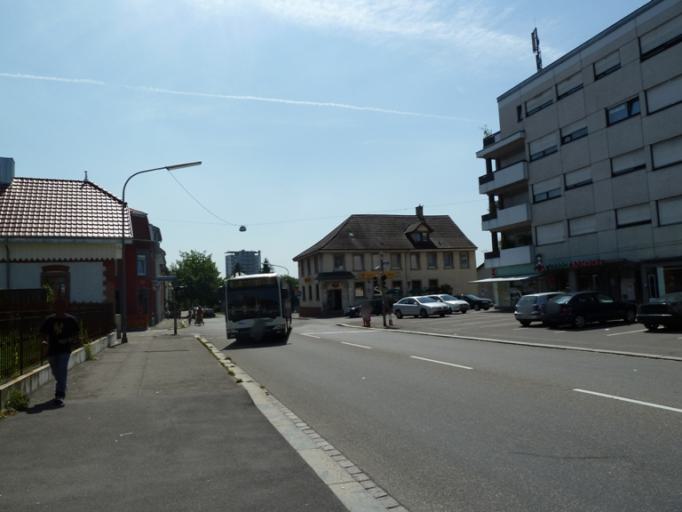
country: DE
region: Baden-Wuerttemberg
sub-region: Freiburg Region
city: Loerrach
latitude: 47.6010
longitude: 7.6586
